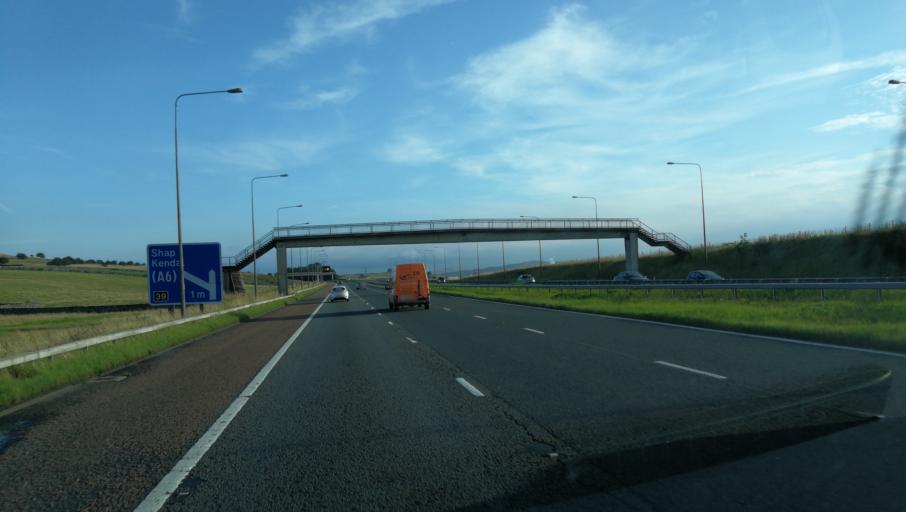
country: GB
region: England
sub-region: Cumbria
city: Penrith
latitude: 54.5273
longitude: -2.6588
